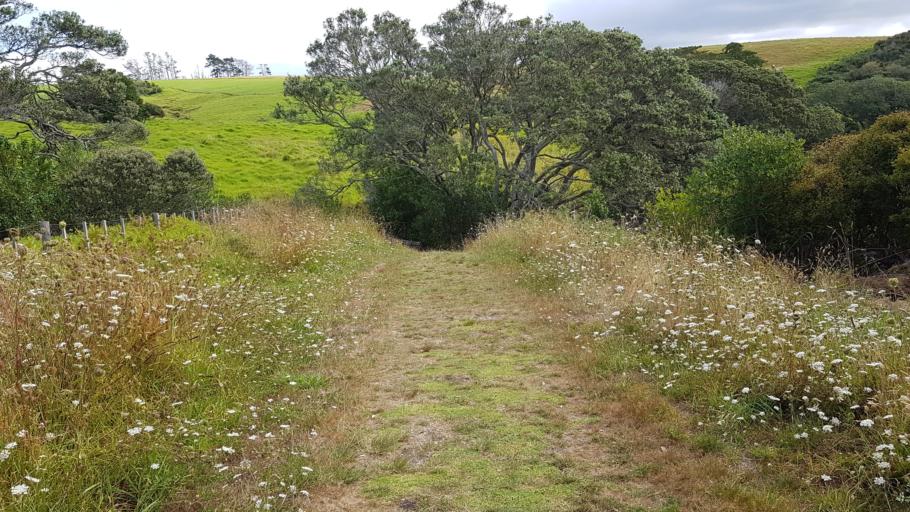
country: NZ
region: Auckland
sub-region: Auckland
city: Rothesay Bay
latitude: -36.6635
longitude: 174.7405
